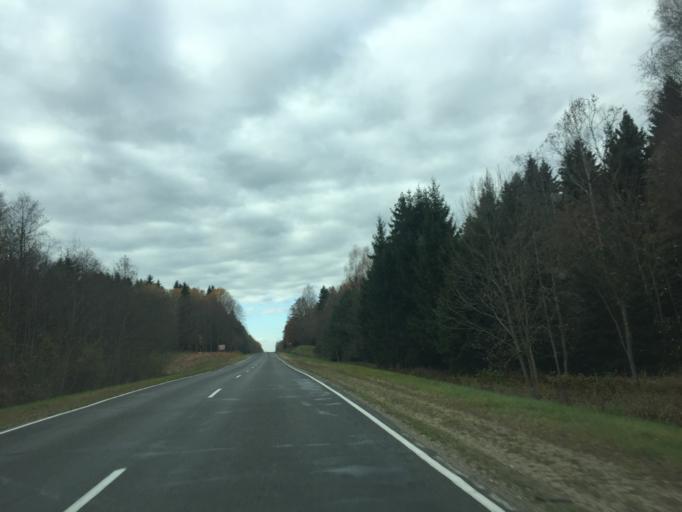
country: BY
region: Vitebsk
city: Mosar
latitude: 55.0672
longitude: 27.3389
